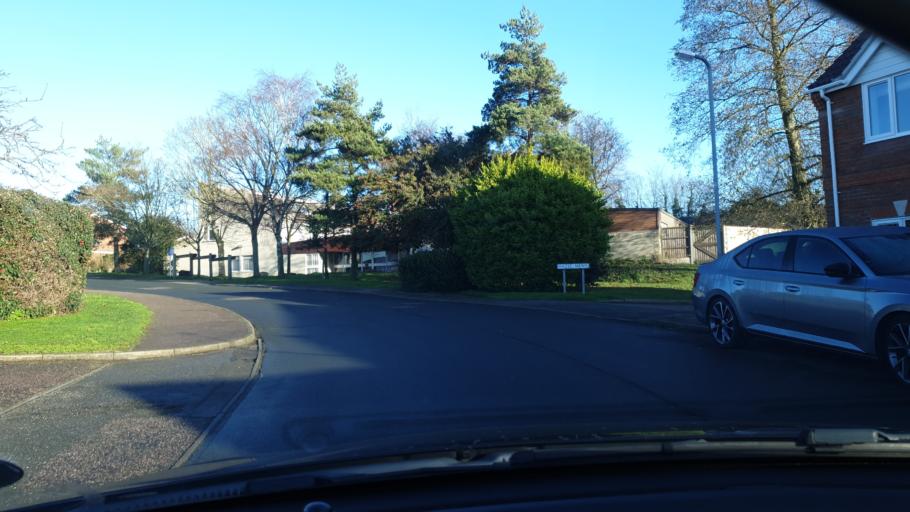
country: GB
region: England
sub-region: Essex
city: Brightlingsea
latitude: 51.8145
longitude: 1.0189
